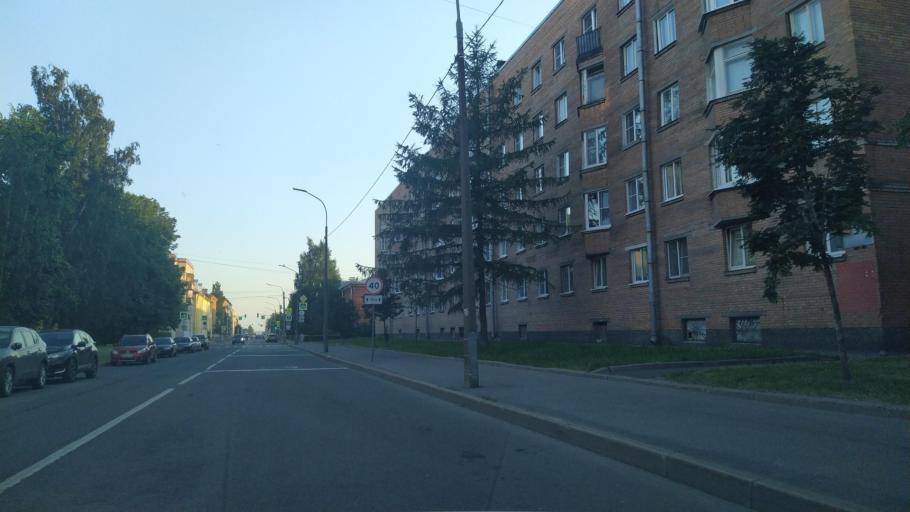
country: RU
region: St.-Petersburg
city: Kronshtadt
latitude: 59.9980
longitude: 29.7596
